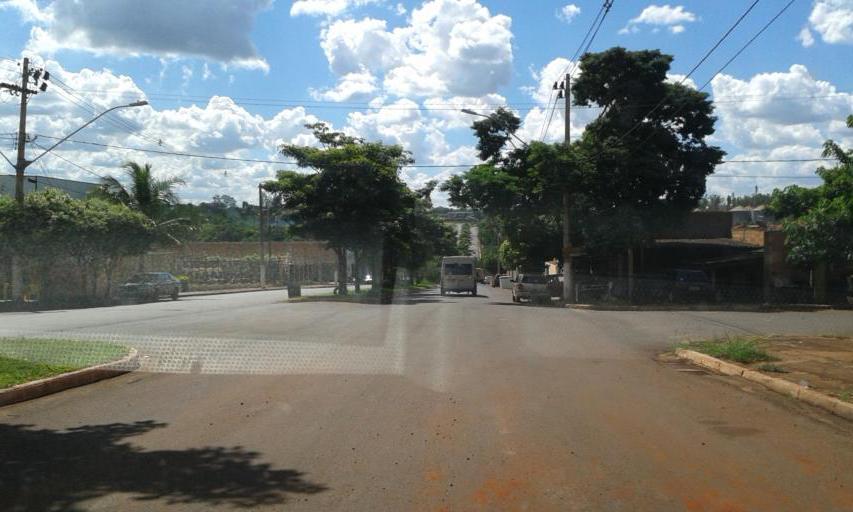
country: BR
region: Minas Gerais
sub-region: Ituiutaba
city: Ituiutaba
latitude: -18.9722
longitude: -49.4860
